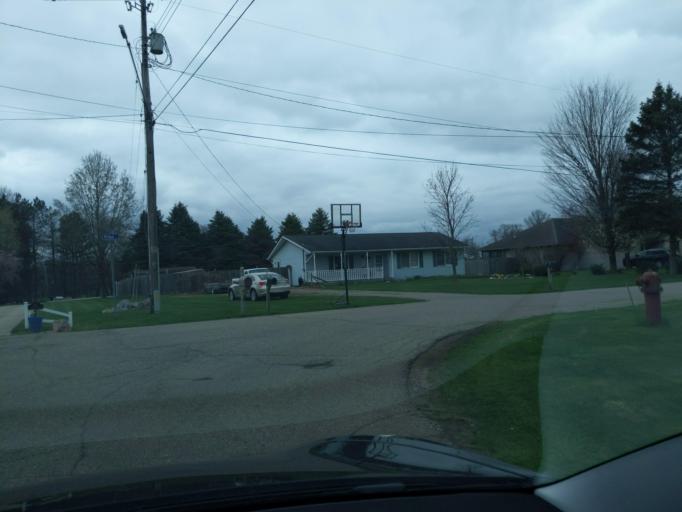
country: US
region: Michigan
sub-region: Ingham County
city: Stockbridge
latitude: 42.4445
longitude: -84.1825
